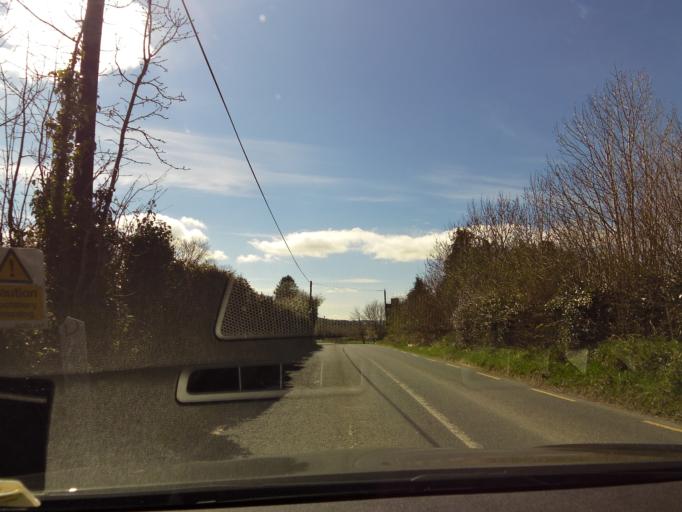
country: IE
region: Leinster
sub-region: Wicklow
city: Aughrim
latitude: 52.8133
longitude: -6.4016
